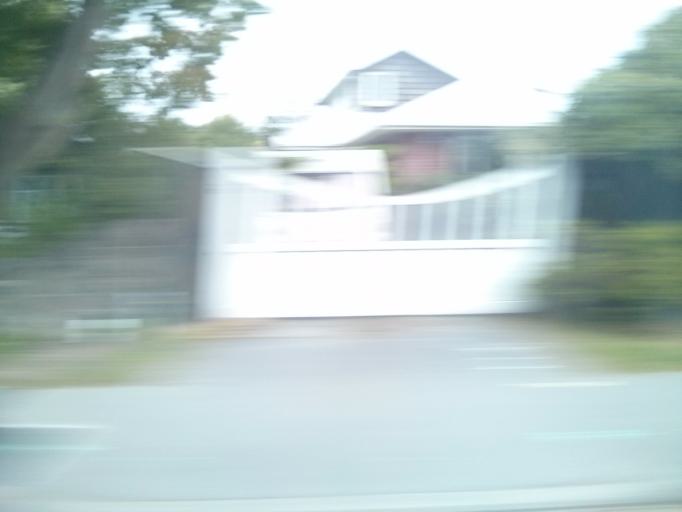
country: NZ
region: Canterbury
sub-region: Christchurch City
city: Christchurch
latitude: -43.5278
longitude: 172.6022
